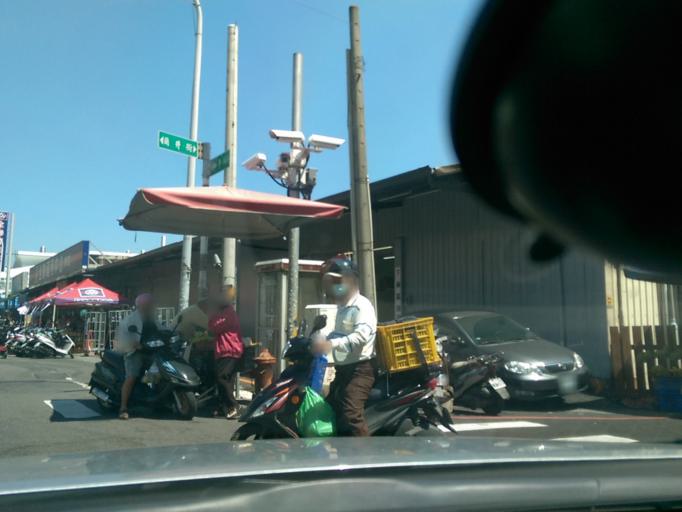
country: TW
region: Taiwan
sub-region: Chiayi
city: Jiayi Shi
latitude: 23.4783
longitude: 120.4574
